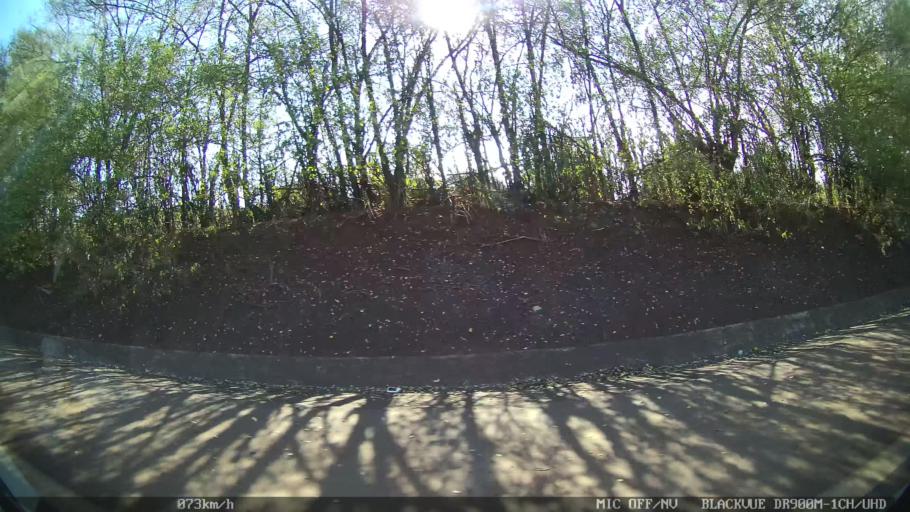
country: BR
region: Sao Paulo
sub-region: Iracemapolis
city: Iracemapolis
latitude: -22.6638
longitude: -47.5330
